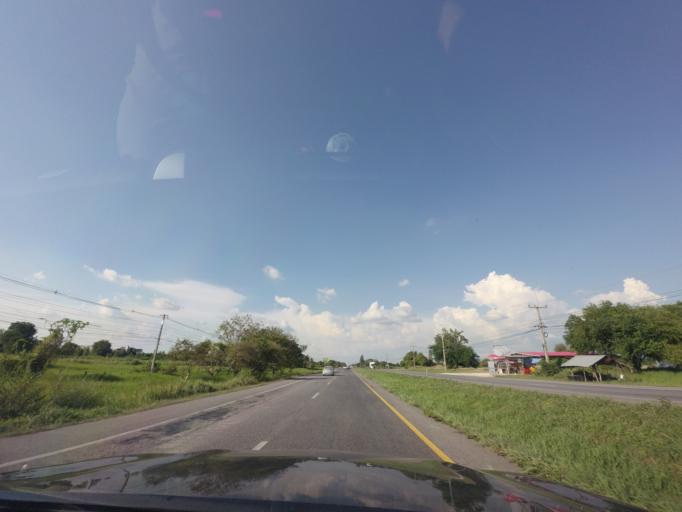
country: TH
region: Khon Kaen
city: Non Sila
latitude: 16.0007
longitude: 102.7018
